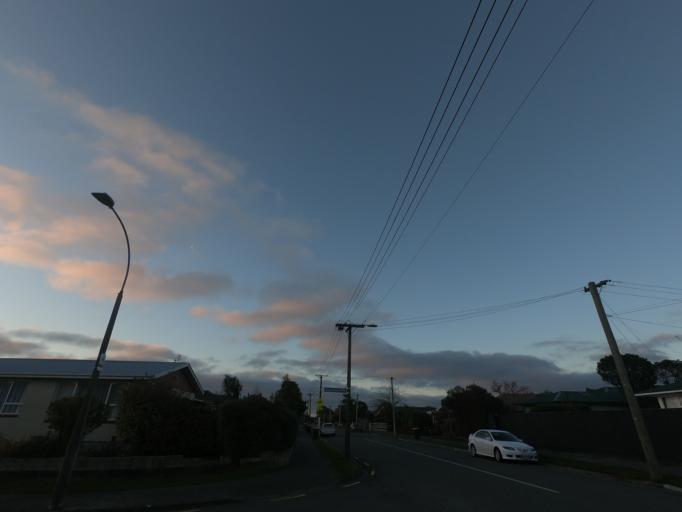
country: NZ
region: Canterbury
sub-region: Selwyn District
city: Prebbleton
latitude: -43.5741
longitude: 172.5680
